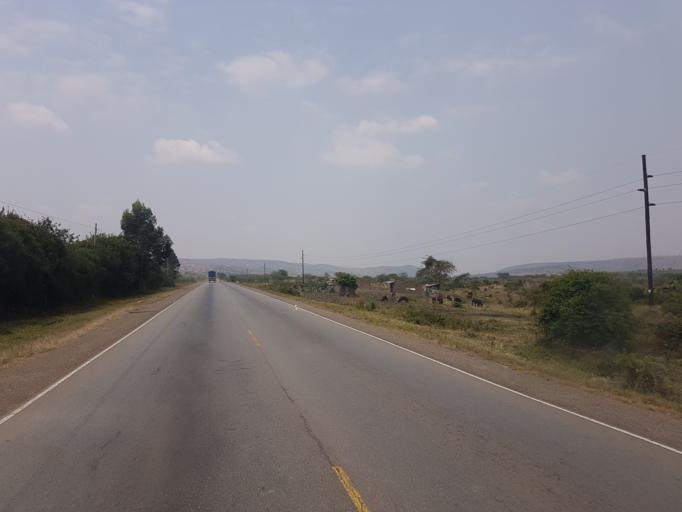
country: UG
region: Western Region
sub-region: Mbarara District
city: Mbarara
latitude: -0.5104
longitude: 30.8242
